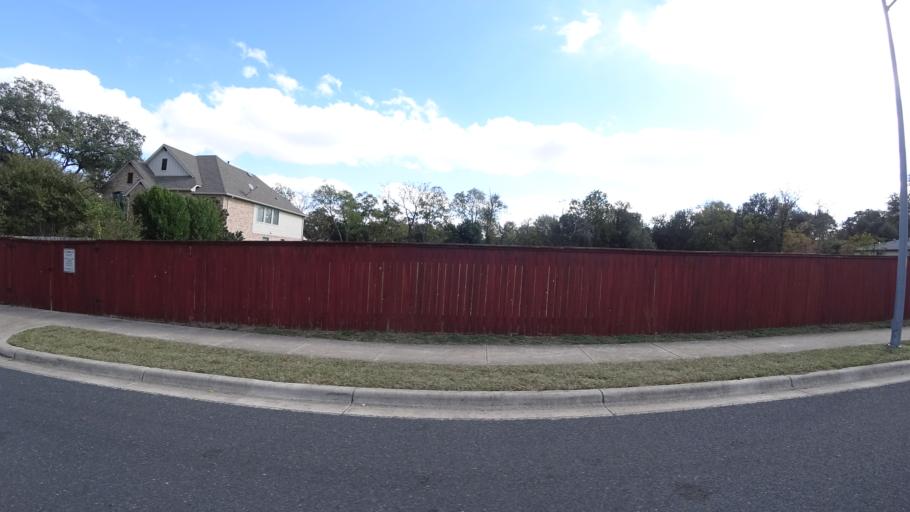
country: US
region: Texas
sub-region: Williamson County
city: Jollyville
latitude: 30.4258
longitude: -97.7283
